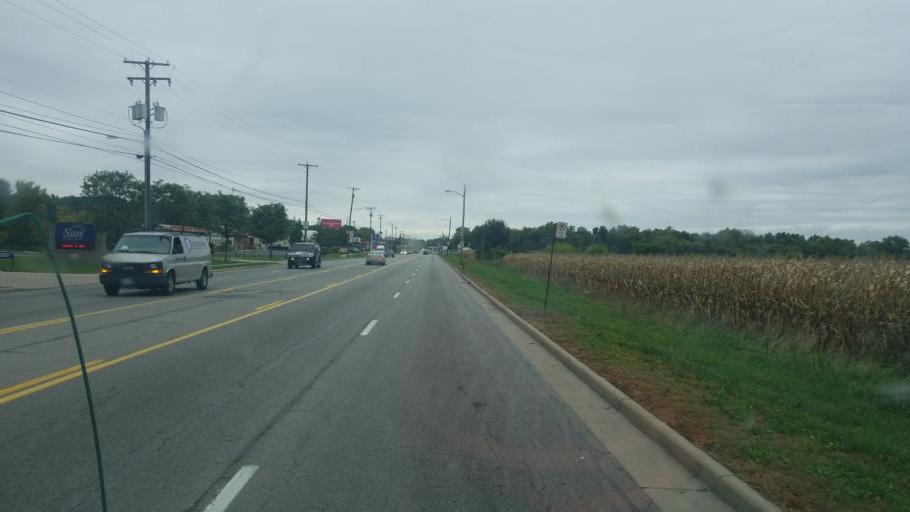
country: US
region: Ohio
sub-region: Lucas County
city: Ottawa Hills
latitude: 41.6421
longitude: -83.6645
